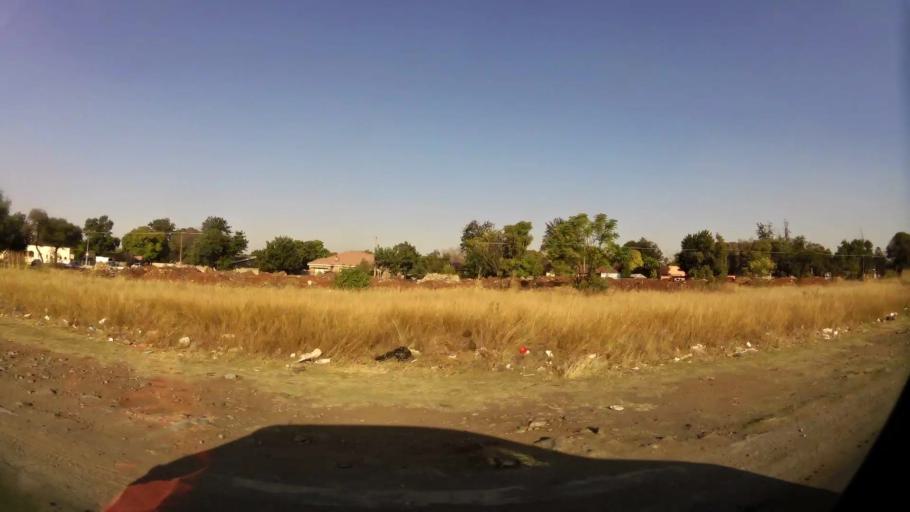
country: ZA
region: North-West
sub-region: Bojanala Platinum District Municipality
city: Rustenburg
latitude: -25.6488
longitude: 27.2251
